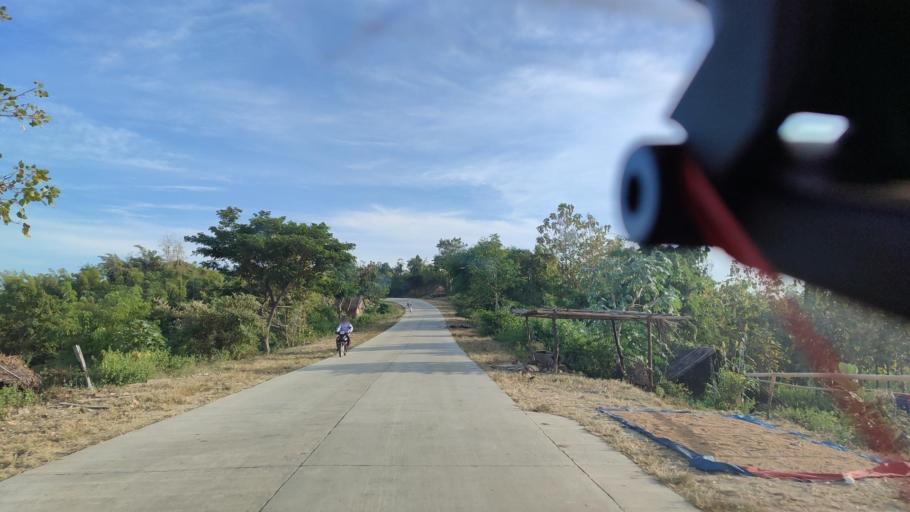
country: MM
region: Magway
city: Taungdwingyi
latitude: 20.0384
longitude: 95.7849
